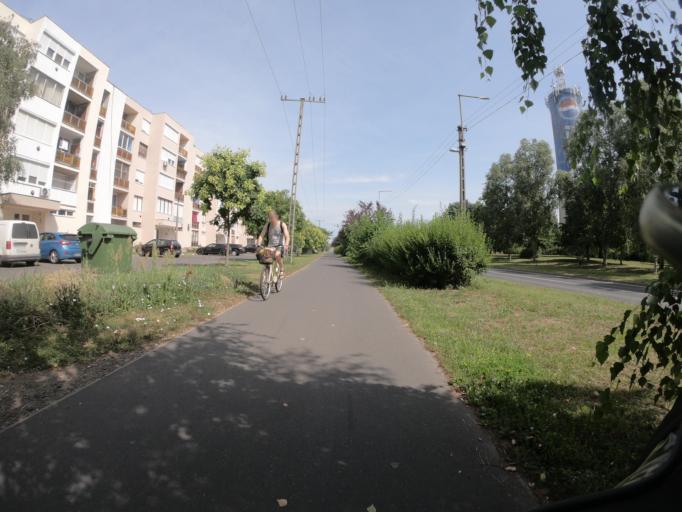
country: HU
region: Jasz-Nagykun-Szolnok
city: Tiszafured
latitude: 47.6193
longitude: 20.7479
